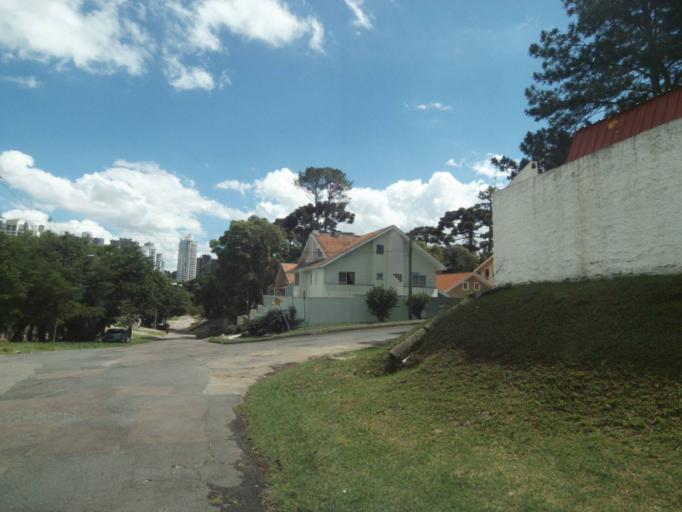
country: BR
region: Parana
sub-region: Curitiba
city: Curitiba
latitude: -25.4322
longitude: -49.3310
